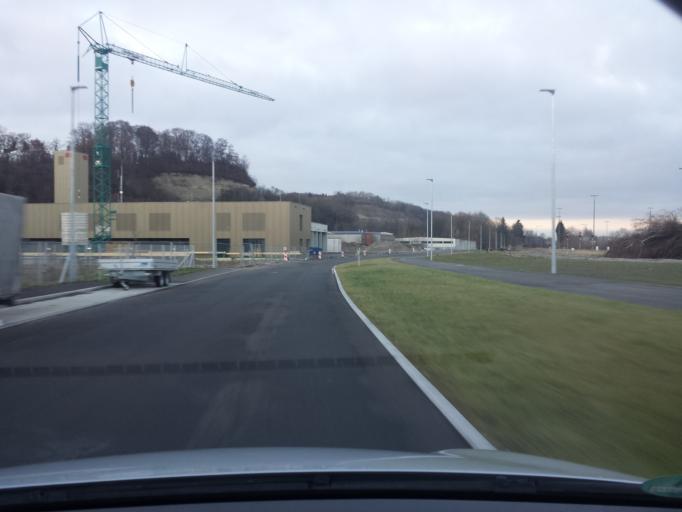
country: DE
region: Baden-Wuerttemberg
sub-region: Tuebingen Region
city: Biberach an der Riss
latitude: 48.1042
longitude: 9.7908
